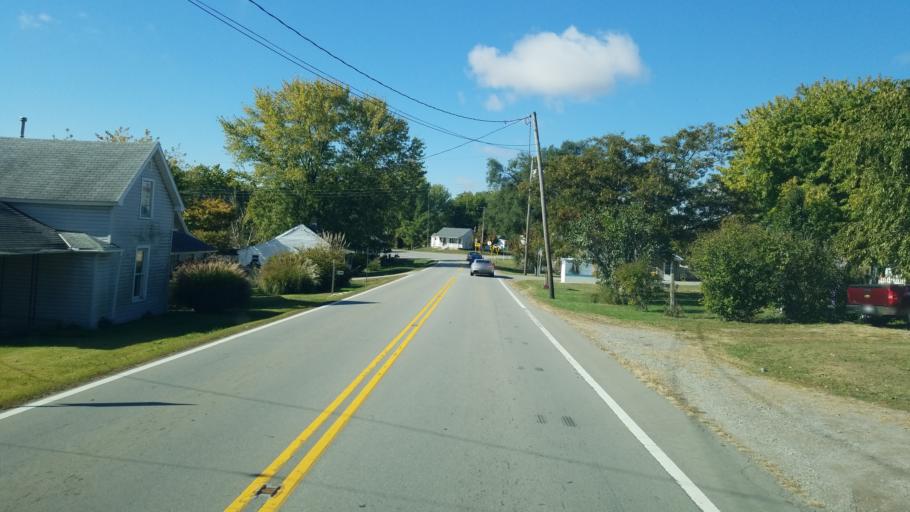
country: US
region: Ohio
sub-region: Fayette County
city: Washington Court House
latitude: 39.4758
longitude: -83.4822
